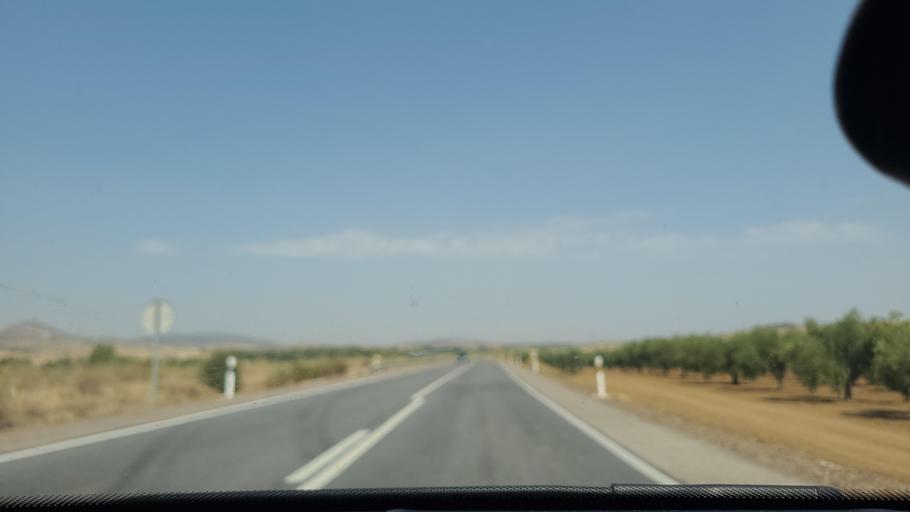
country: ES
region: Extremadura
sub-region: Provincia de Badajoz
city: Fuente del Maestre
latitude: 38.4861
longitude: -6.4820
